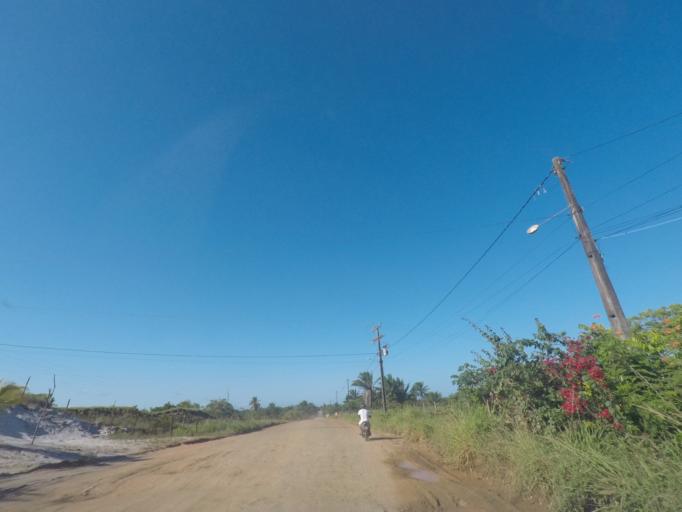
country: BR
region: Bahia
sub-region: Marau
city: Marau
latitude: -14.0371
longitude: -38.9550
